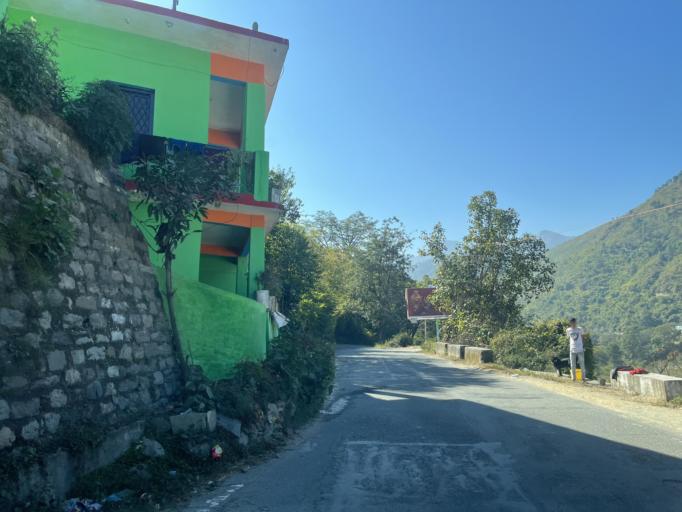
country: IN
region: Uttarakhand
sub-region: Almora
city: Ranikhet
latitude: 29.5235
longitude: 79.4825
